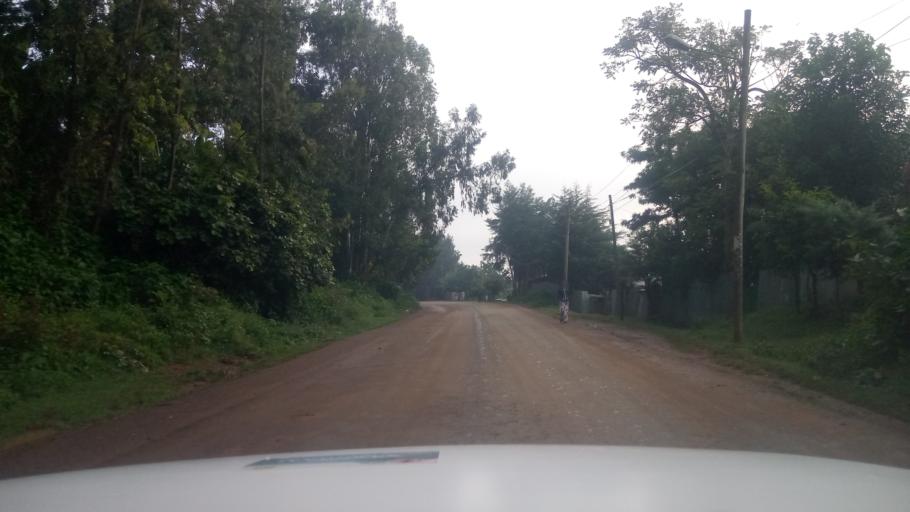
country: ET
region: Oromiya
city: Jima
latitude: 7.6804
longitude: 36.8342
